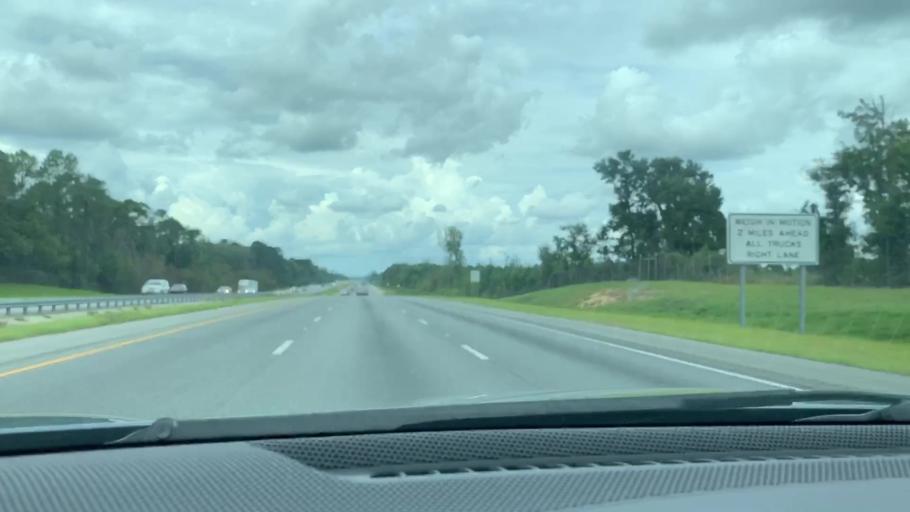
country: US
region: Georgia
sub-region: McIntosh County
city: Darien
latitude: 31.4349
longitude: -81.4438
